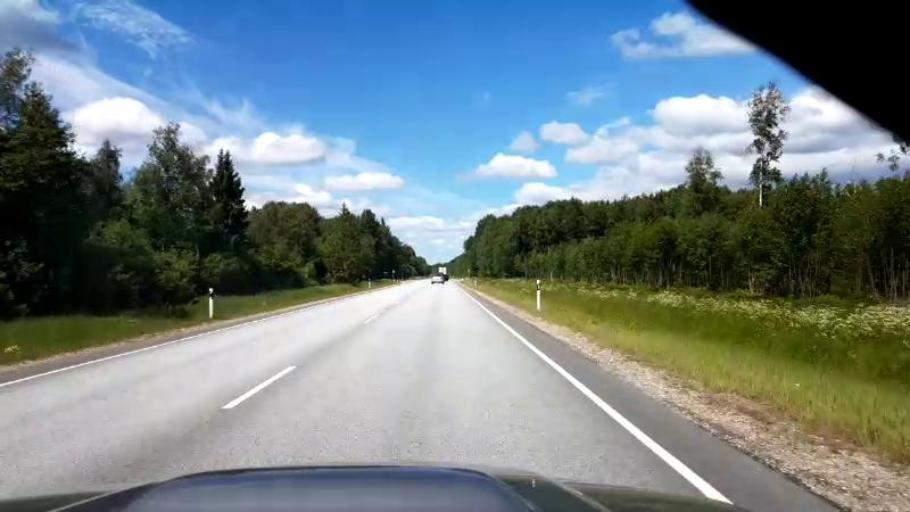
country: EE
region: Paernumaa
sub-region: Halinga vald
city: Parnu-Jaagupi
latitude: 58.5430
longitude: 24.5419
